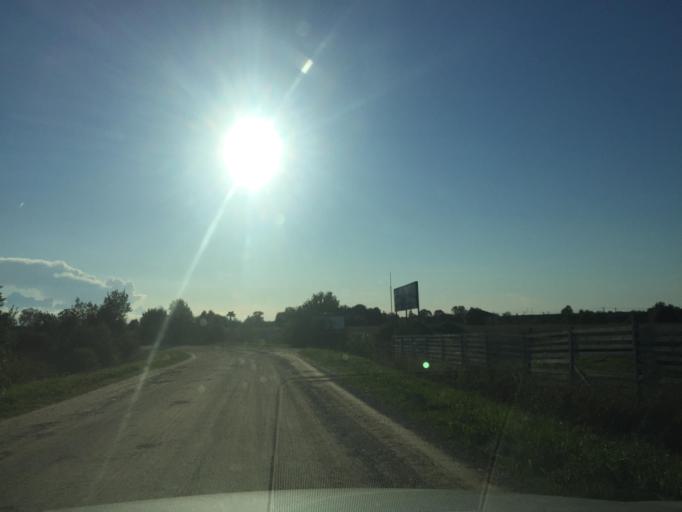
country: RU
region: Leningrad
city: Rozhdestveno
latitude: 59.3328
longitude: 30.0009
